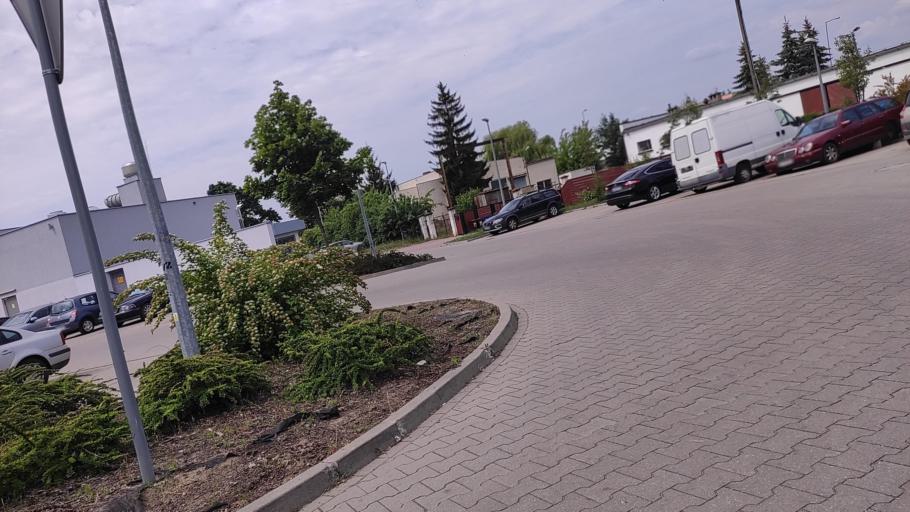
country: PL
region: Greater Poland Voivodeship
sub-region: Powiat poznanski
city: Swarzedz
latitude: 52.4016
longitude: 17.0611
